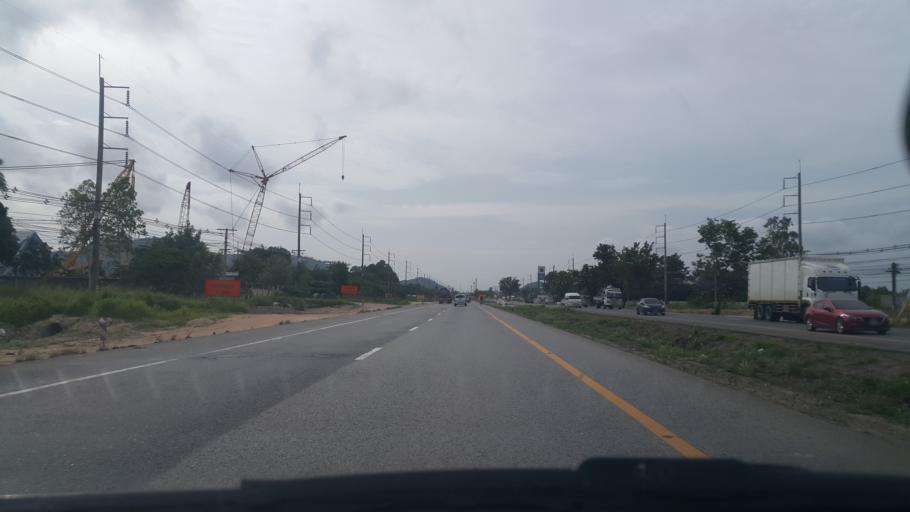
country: TH
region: Rayong
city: Nikhom Phattana
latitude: 12.8034
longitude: 101.1463
